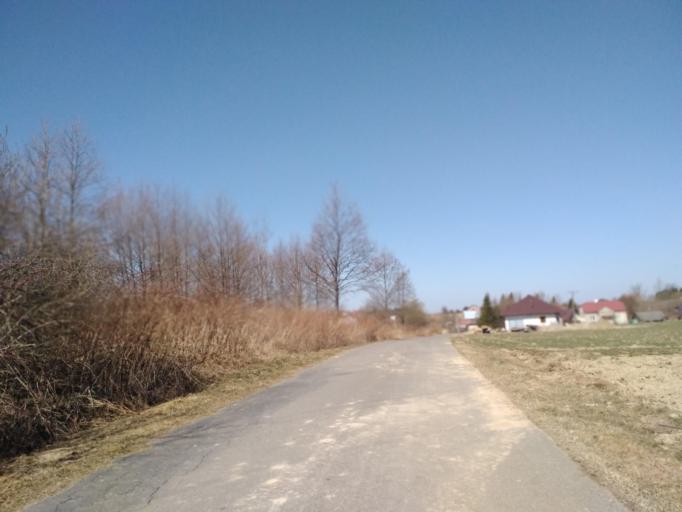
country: PL
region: Subcarpathian Voivodeship
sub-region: Powiat brzozowski
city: Orzechowka
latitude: 49.7124
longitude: 21.9678
